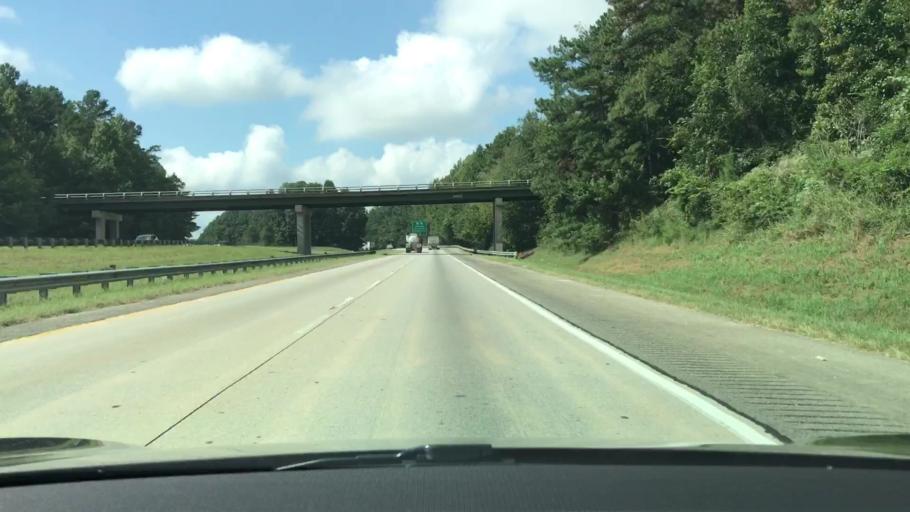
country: US
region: Georgia
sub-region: Hall County
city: Gainesville
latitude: 34.2470
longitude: -83.8342
